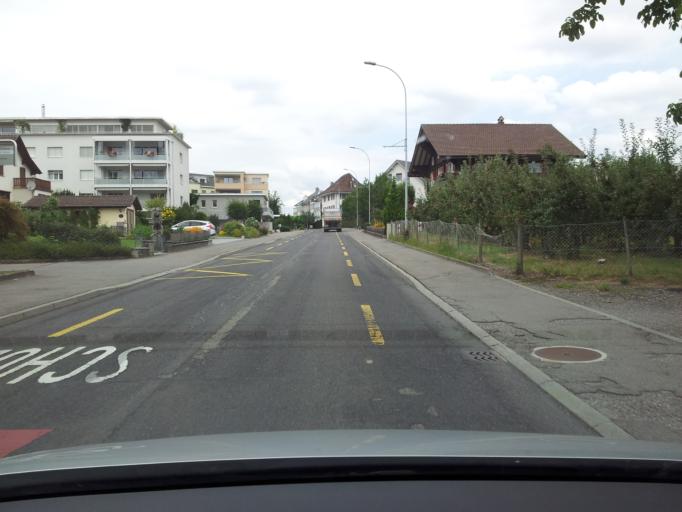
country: CH
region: Lucerne
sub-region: Sursee District
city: Oberkirch
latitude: 47.1588
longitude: 8.1156
